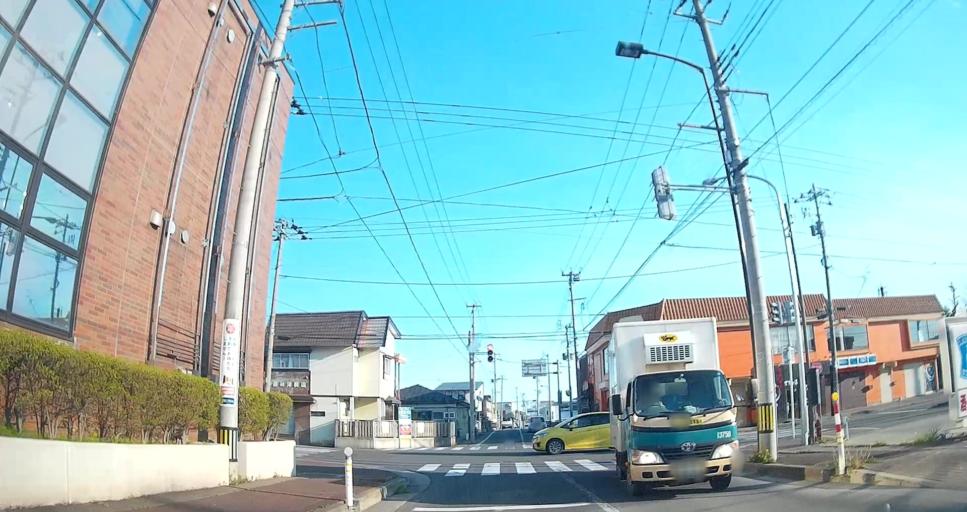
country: JP
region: Aomori
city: Mutsu
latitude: 41.2937
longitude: 141.2104
